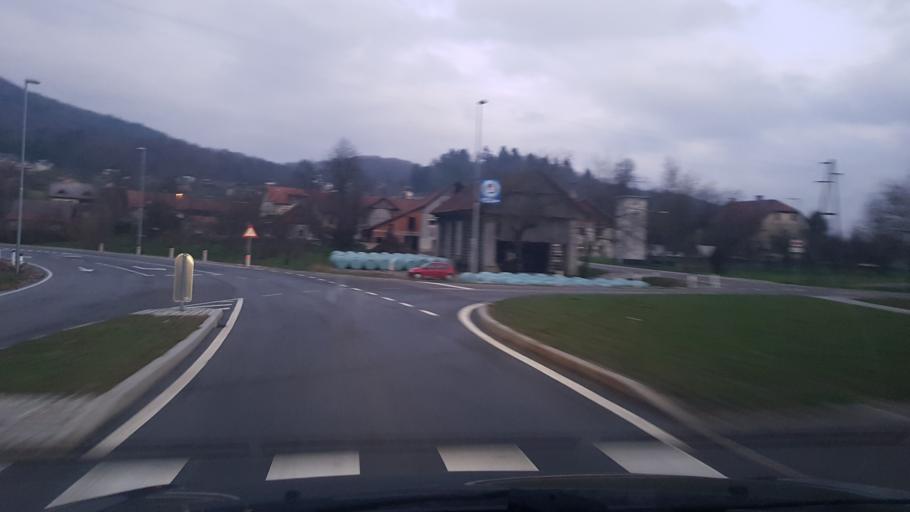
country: SI
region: Idrija
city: Idrija
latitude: 45.9576
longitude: 14.0899
